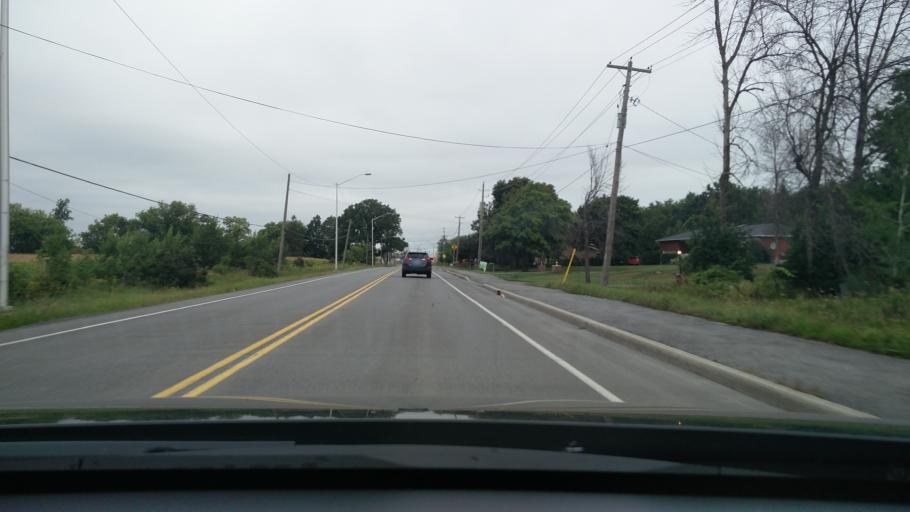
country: CA
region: Ontario
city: Bells Corners
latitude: 45.2634
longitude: -75.7422
